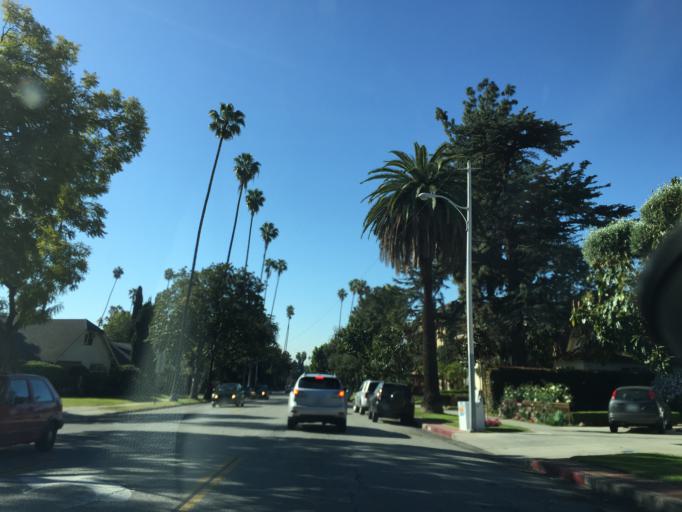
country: US
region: California
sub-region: Los Angeles County
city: South Pasadena
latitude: 34.1067
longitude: -118.1530
